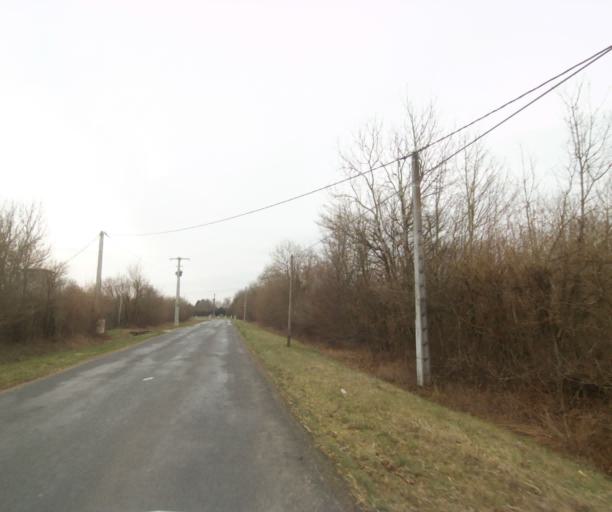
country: FR
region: Champagne-Ardenne
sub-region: Departement de la Haute-Marne
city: Villiers-en-Lieu
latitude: 48.6497
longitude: 4.8742
